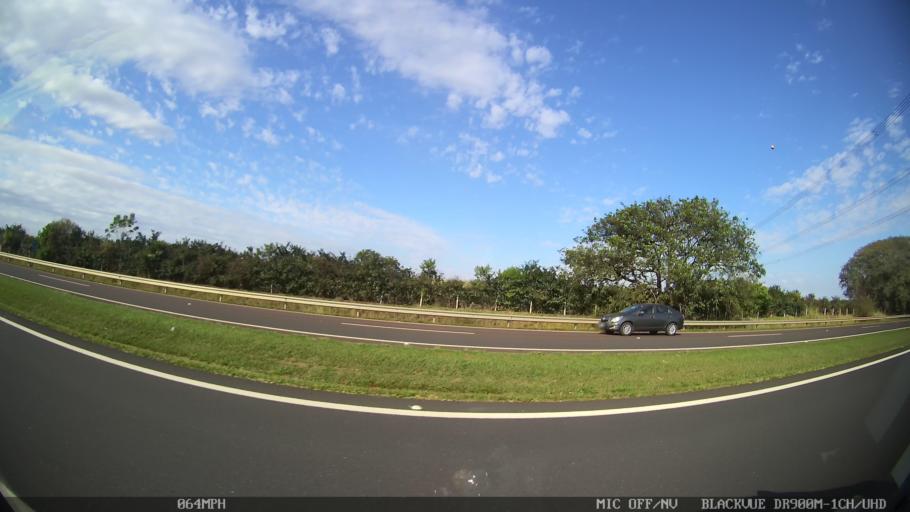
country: BR
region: Sao Paulo
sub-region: Iracemapolis
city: Iracemapolis
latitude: -22.6463
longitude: -47.5115
